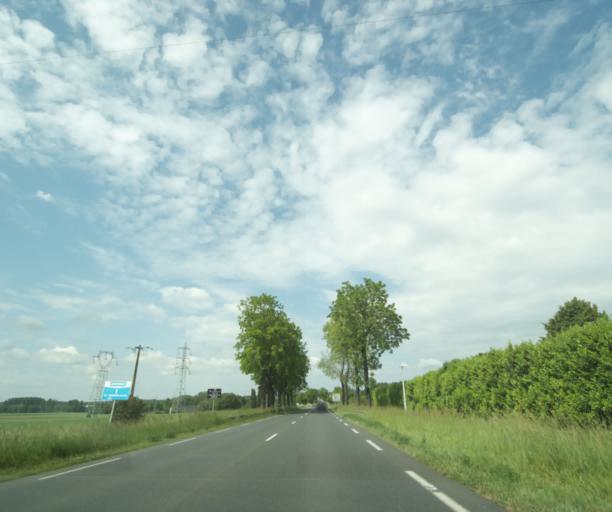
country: FR
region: Pays de la Loire
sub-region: Departement de Maine-et-Loire
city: Distre
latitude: 47.2112
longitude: -0.1173
